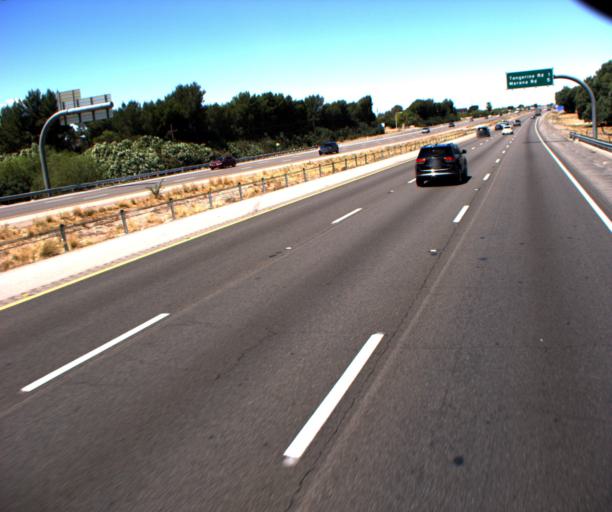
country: US
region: Arizona
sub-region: Pima County
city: Marana
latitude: 32.4109
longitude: -111.1450
